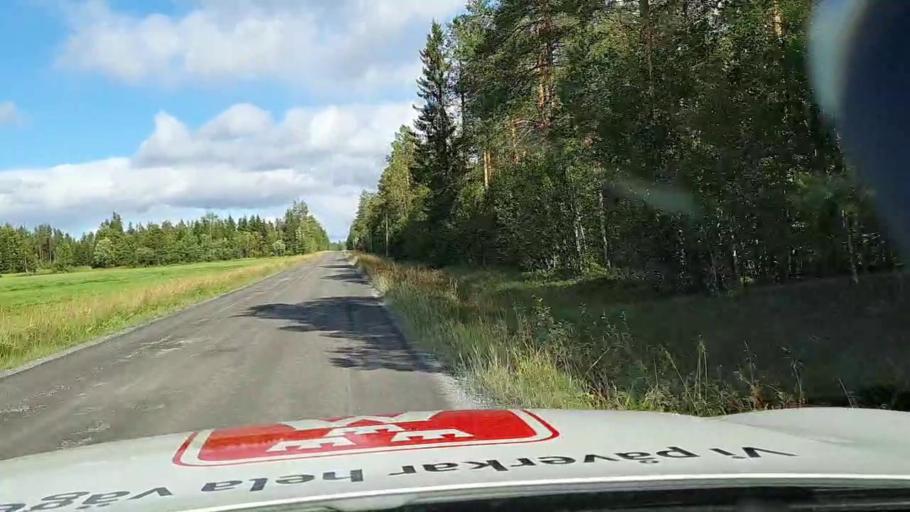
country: SE
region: Jaemtland
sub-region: Stroemsunds Kommun
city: Stroemsund
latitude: 63.6866
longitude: 15.1228
